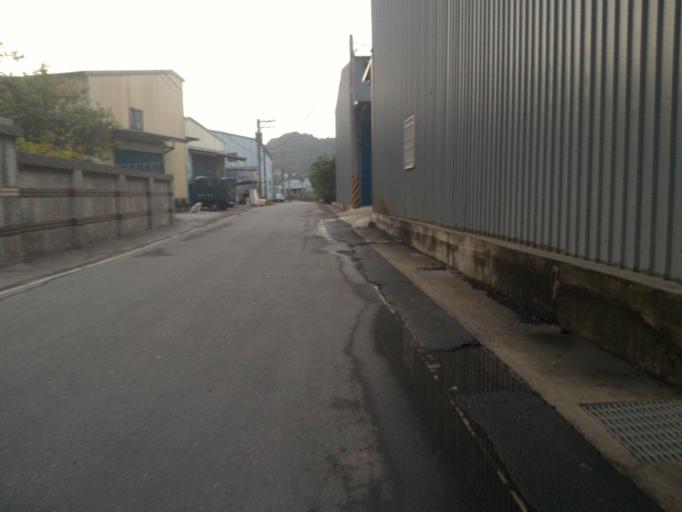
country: TW
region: Taipei
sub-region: Taipei
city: Banqiao
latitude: 24.9562
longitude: 121.4040
